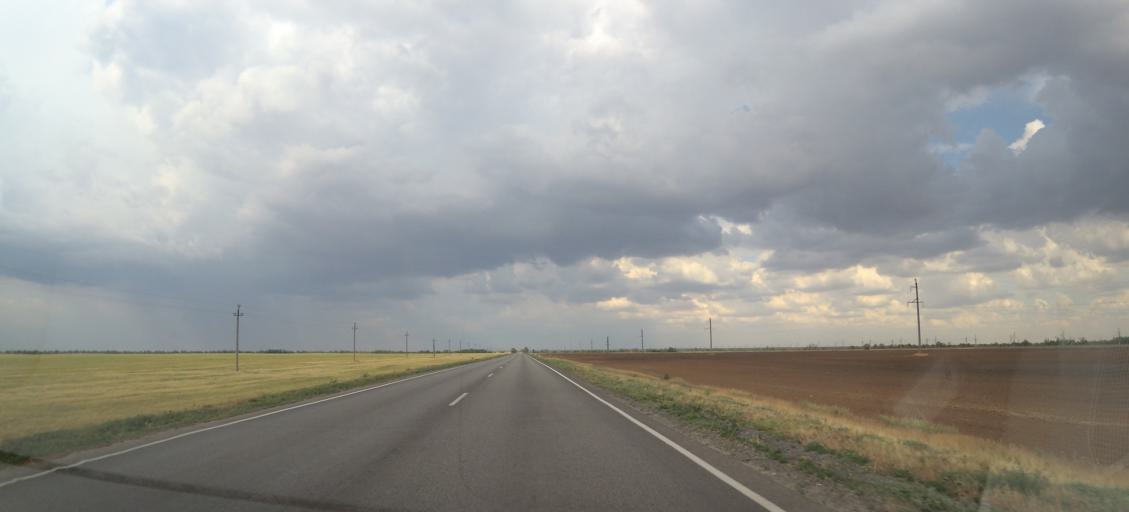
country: RU
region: Rostov
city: Zimovniki
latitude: 47.1205
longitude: 42.3908
